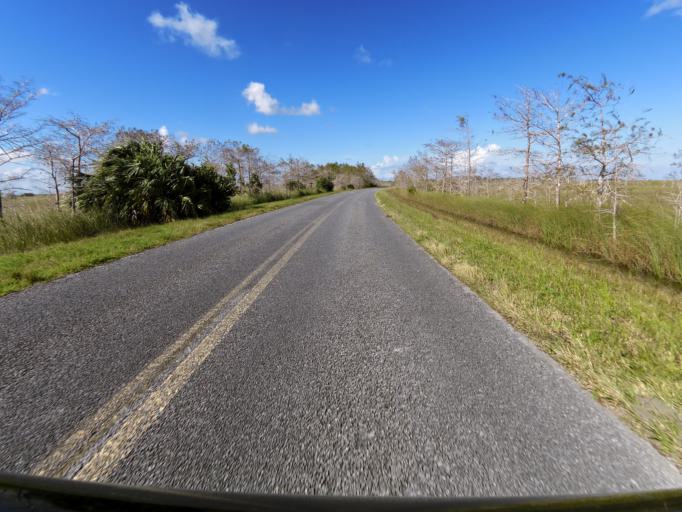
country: US
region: Florida
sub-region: Miami-Dade County
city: Florida City
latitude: 25.4336
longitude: -80.7800
